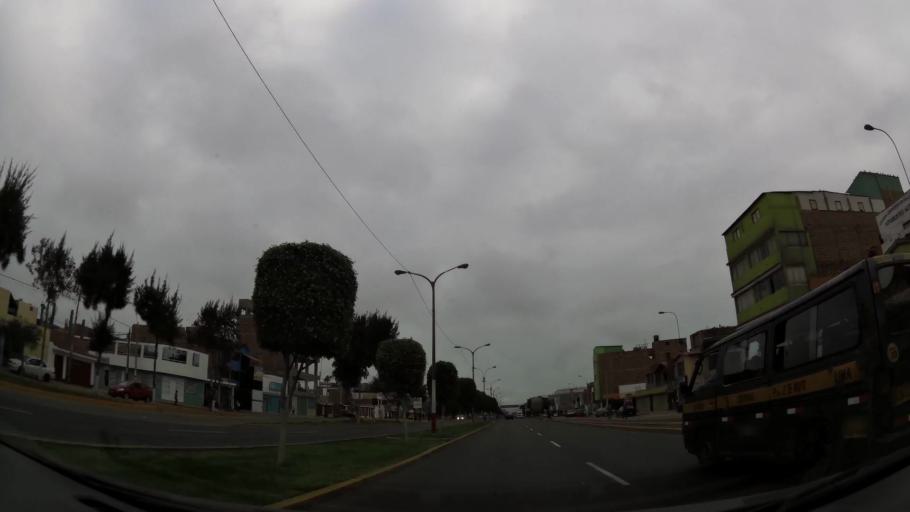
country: PE
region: Callao
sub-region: Callao
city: Callao
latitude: -12.0563
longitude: -77.1119
